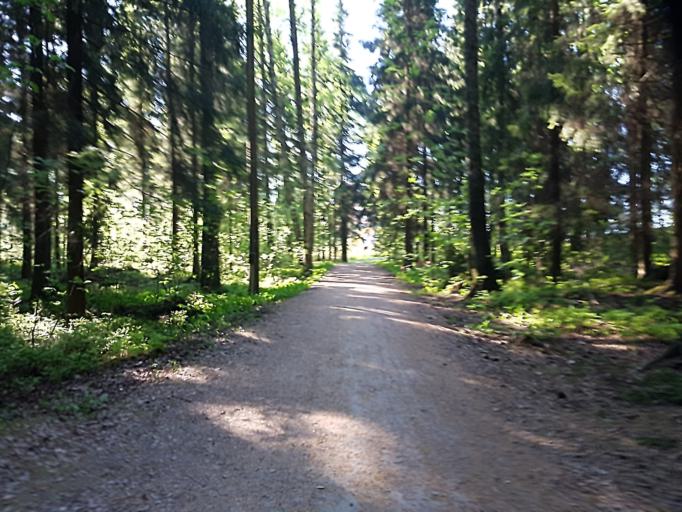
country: FI
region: Uusimaa
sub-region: Helsinki
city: Helsinki
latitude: 60.2218
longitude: 24.9278
